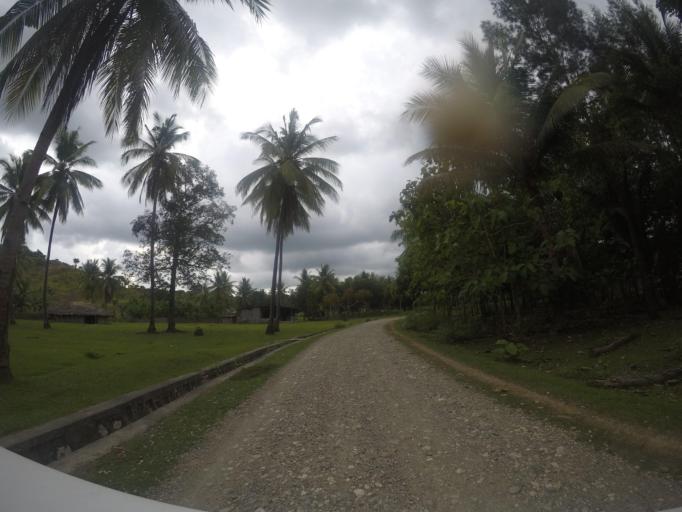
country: TL
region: Viqueque
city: Viqueque
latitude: -8.8599
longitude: 126.3586
